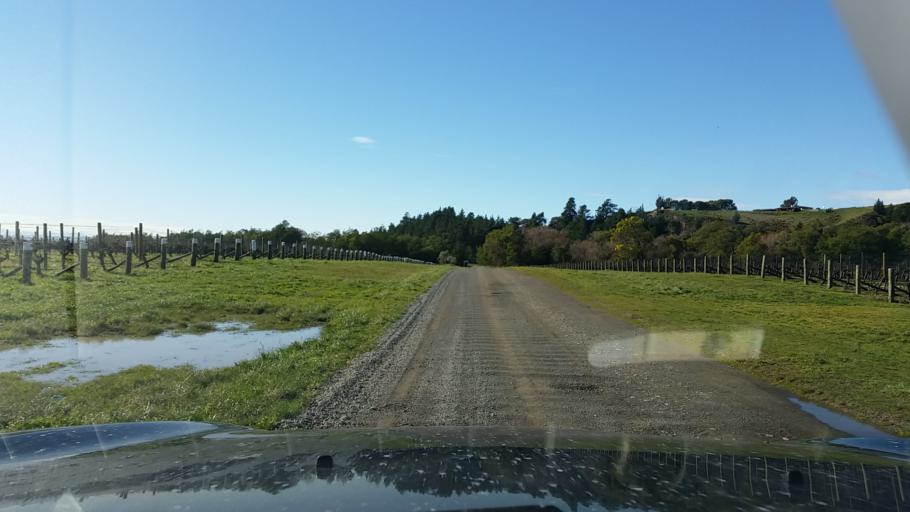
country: NZ
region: Marlborough
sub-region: Marlborough District
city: Blenheim
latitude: -41.5298
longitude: 173.7979
